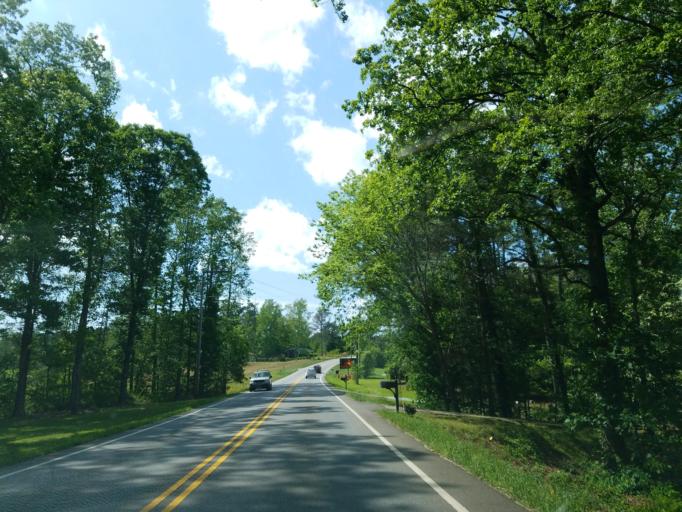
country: US
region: Georgia
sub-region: Cherokee County
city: Ball Ground
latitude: 34.2731
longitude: -84.2963
